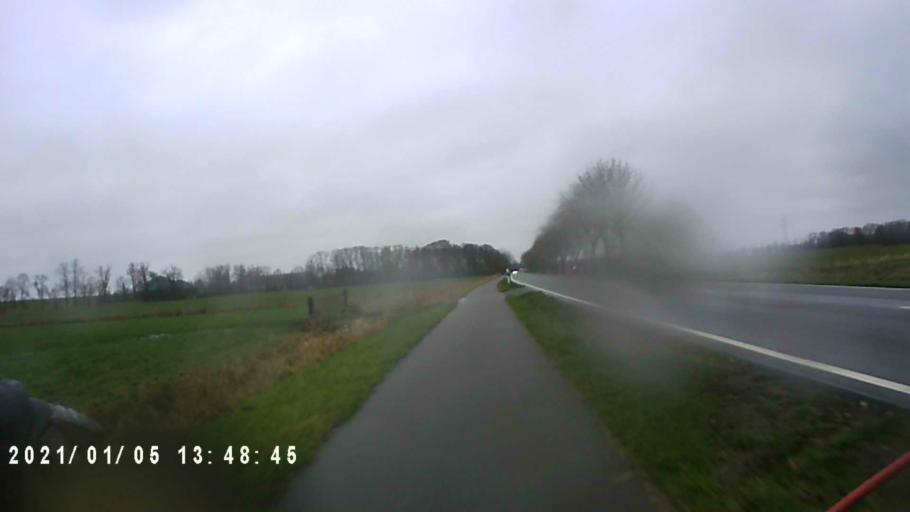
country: DE
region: Lower Saxony
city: Weener
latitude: 53.1788
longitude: 7.3735
